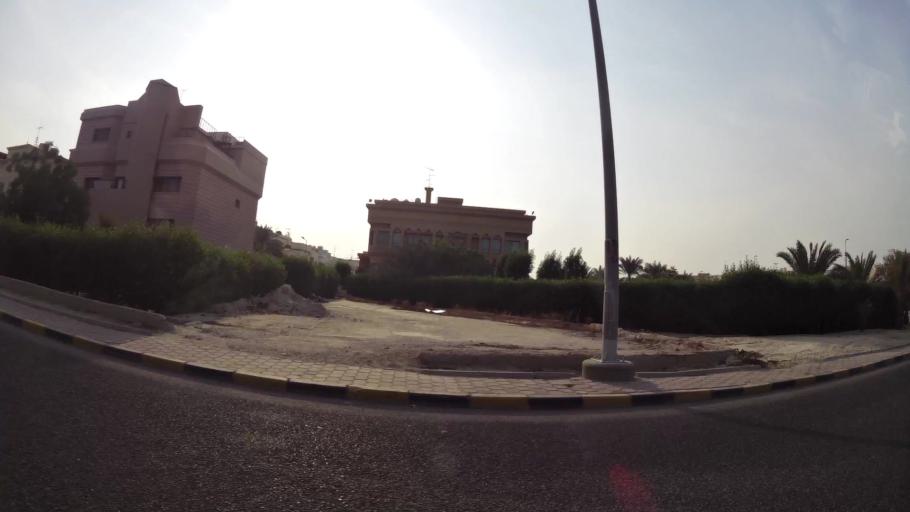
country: KW
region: Mubarak al Kabir
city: Sabah as Salim
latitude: 29.2202
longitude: 48.0616
